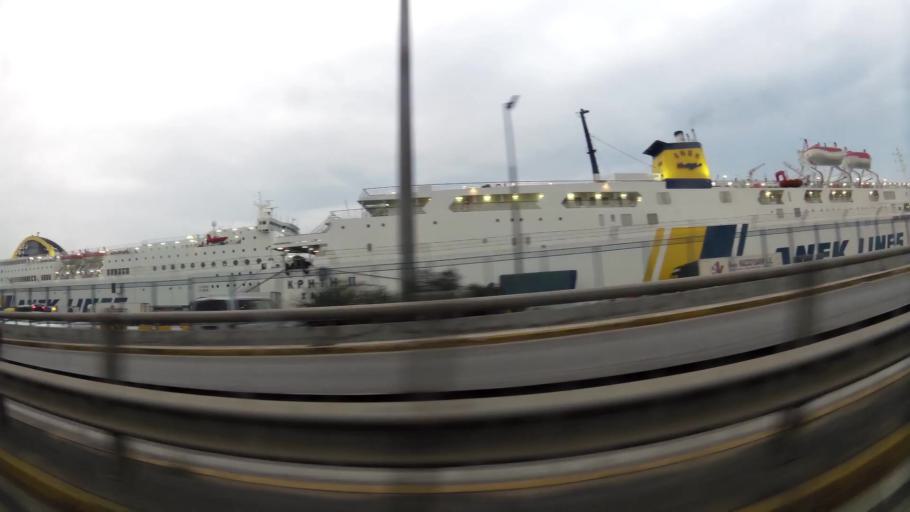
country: GR
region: Attica
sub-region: Nomos Attikis
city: Piraeus
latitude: 37.9467
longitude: 23.6361
